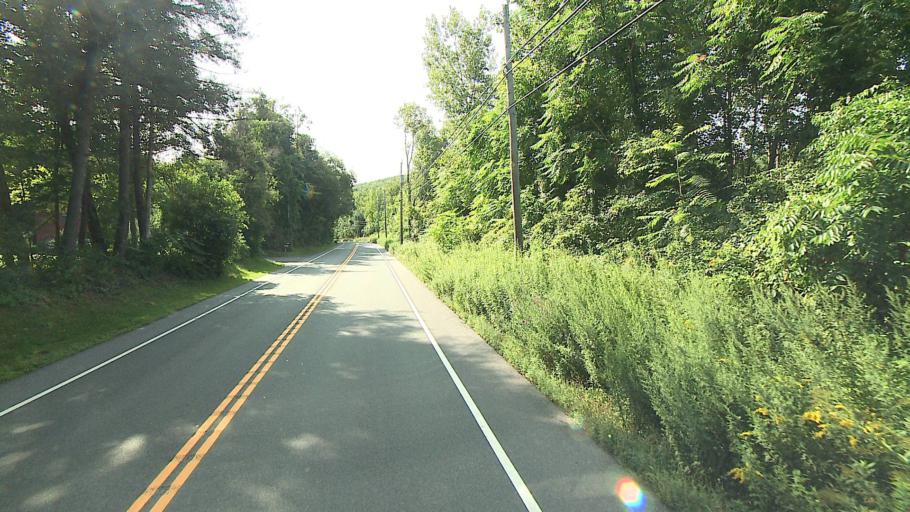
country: US
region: Connecticut
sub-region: Fairfield County
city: Sherman
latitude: 41.6233
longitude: -73.4644
